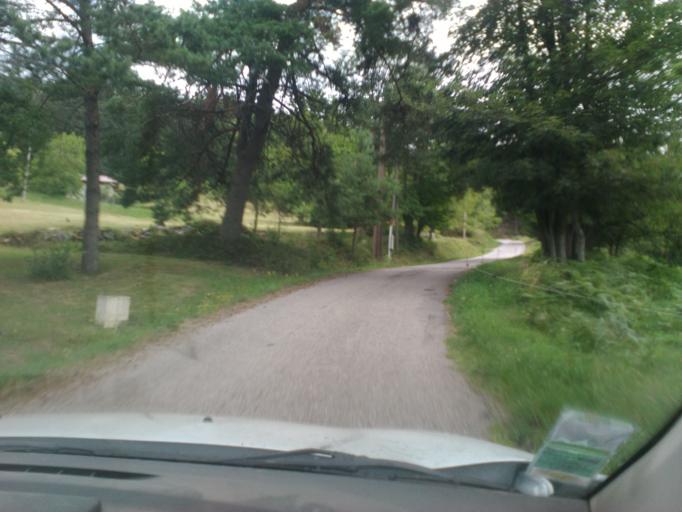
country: FR
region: Lorraine
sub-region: Departement des Vosges
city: Le Tholy
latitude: 48.0952
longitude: 6.7188
